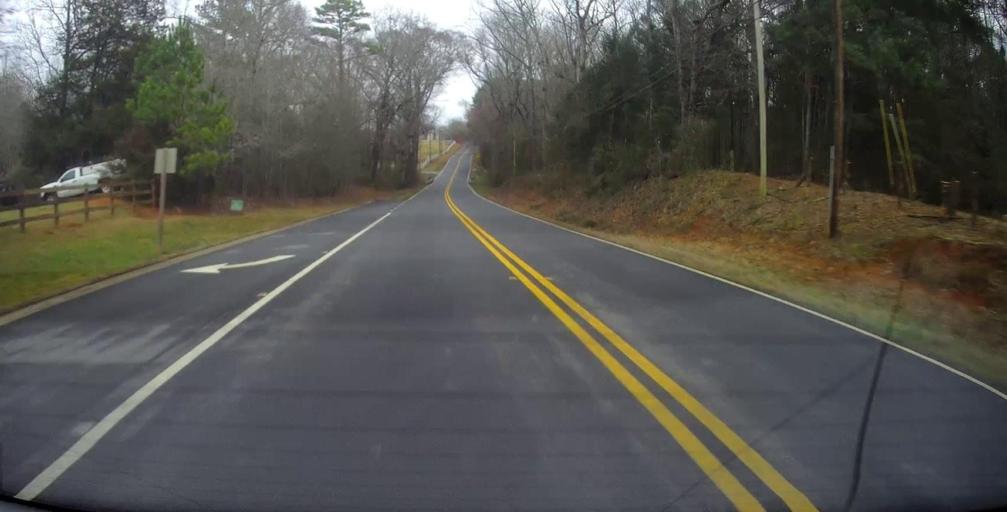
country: US
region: Georgia
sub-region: Pike County
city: Zebulon
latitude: 33.0576
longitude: -84.2702
